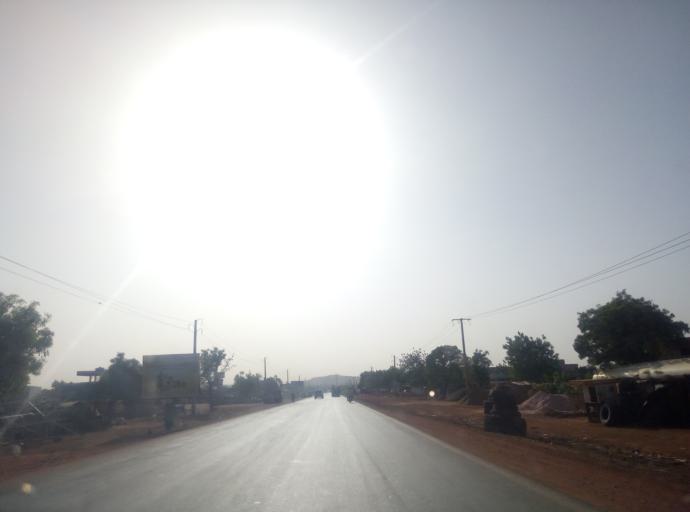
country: ML
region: Bamako
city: Bamako
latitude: 12.5854
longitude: -7.8271
